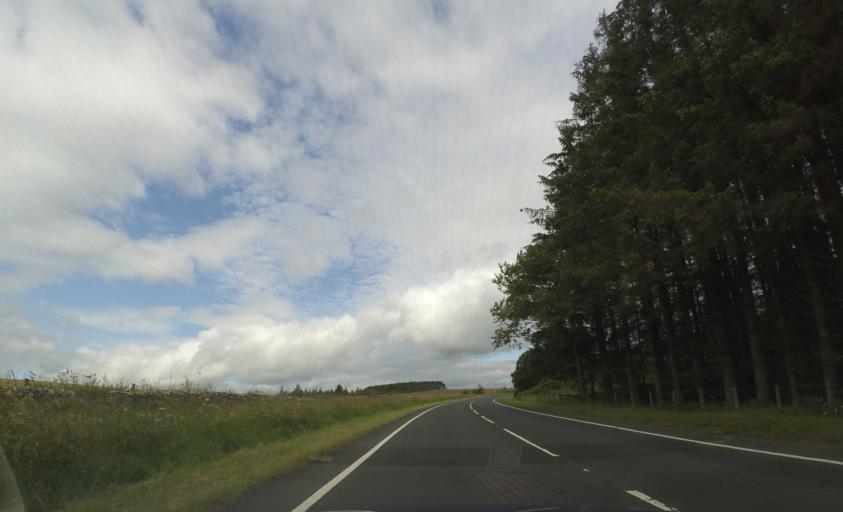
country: GB
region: Scotland
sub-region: The Scottish Borders
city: Selkirk
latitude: 55.5062
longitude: -2.8418
